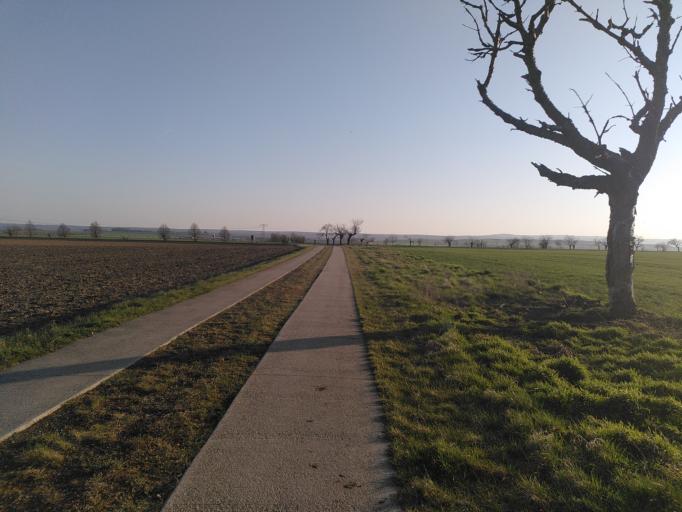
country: DE
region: Saxony-Anhalt
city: Gatersleben
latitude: 51.8001
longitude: 11.2599
